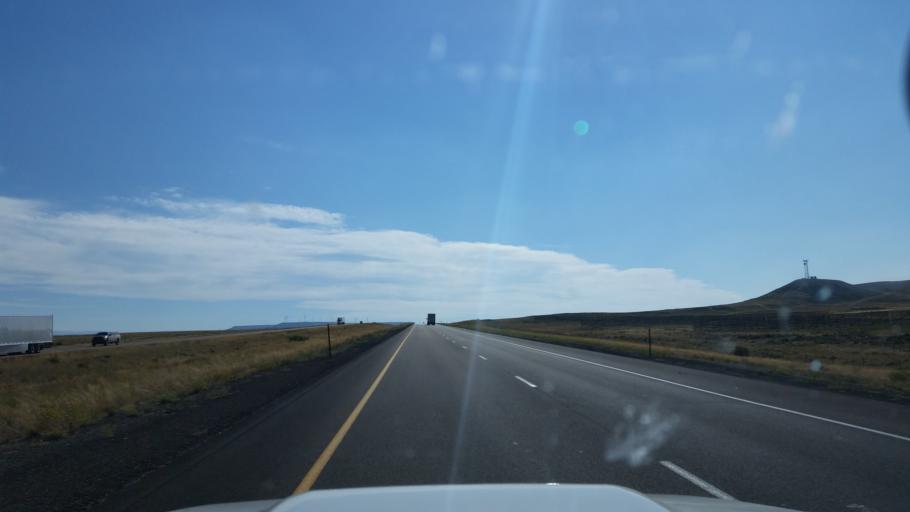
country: US
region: Wyoming
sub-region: Uinta County
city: Lyman
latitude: 41.3511
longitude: -110.3787
